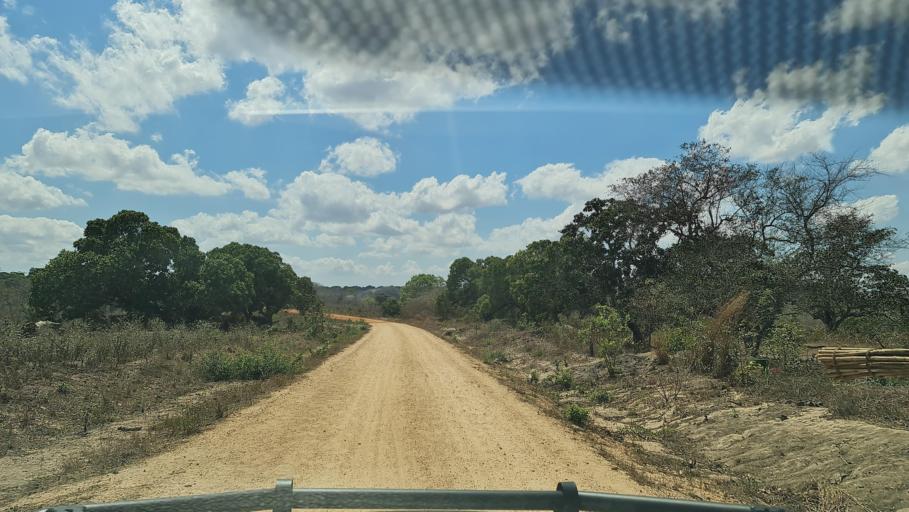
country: MZ
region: Nampula
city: Nacala
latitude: -14.1737
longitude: 40.2403
